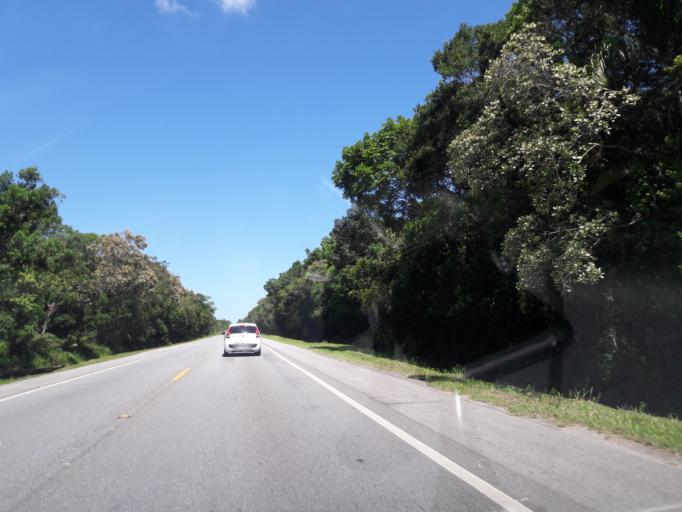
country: BR
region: Parana
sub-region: Pontal Do Parana
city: Pontal do Parana
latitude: -25.6102
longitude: -48.5521
